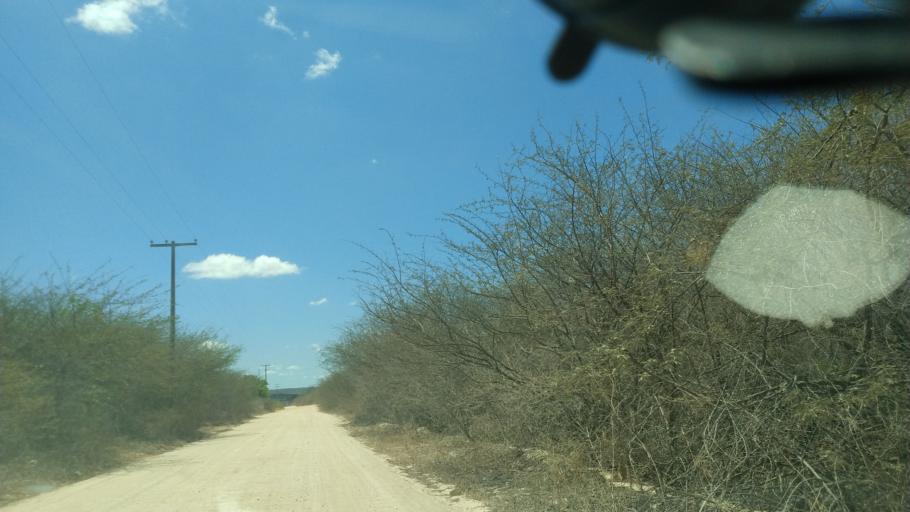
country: BR
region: Rio Grande do Norte
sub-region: Cerro Cora
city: Cerro Cora
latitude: -6.0259
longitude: -36.3358
